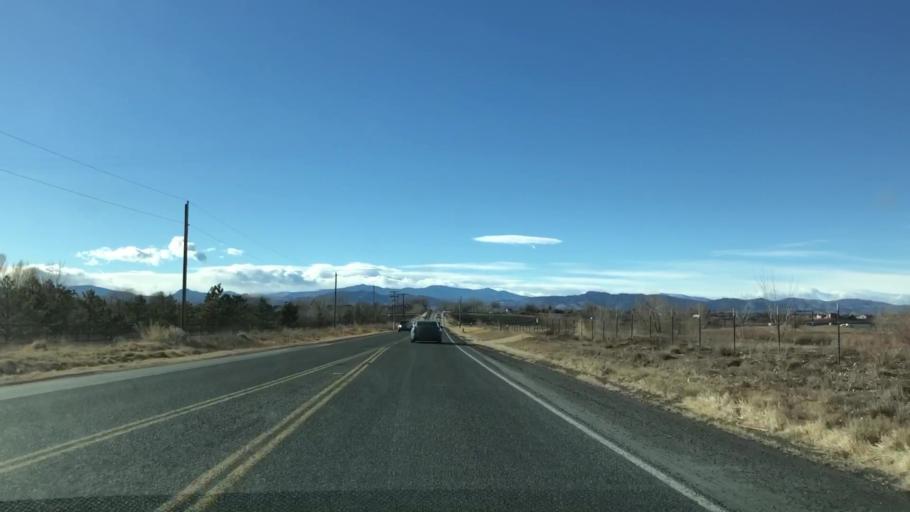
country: US
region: Colorado
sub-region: Weld County
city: Windsor
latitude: 40.5085
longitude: -104.9853
